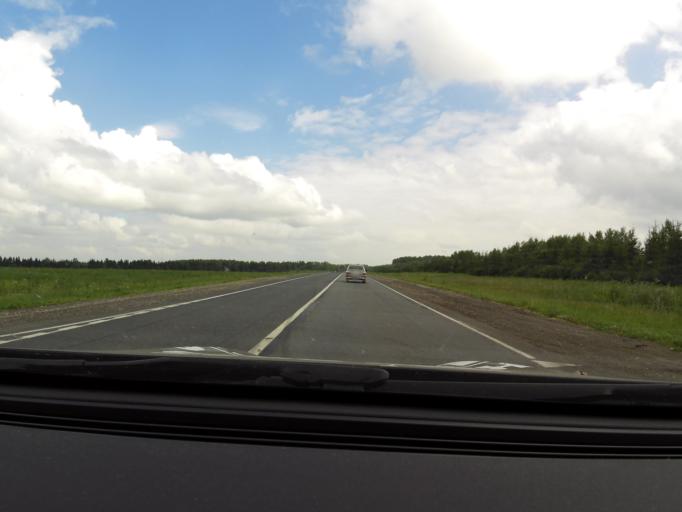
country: RU
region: Perm
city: Suksun
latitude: 57.1610
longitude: 57.2338
